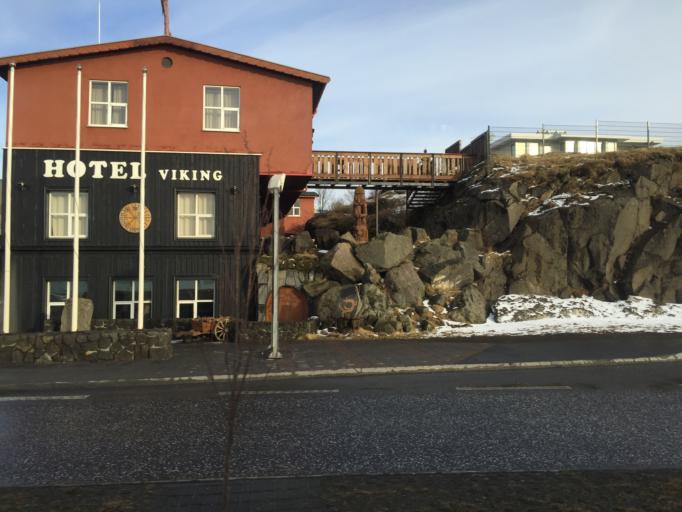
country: IS
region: Capital Region
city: Hafnarfjoerdur
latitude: 64.0650
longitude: -21.9567
